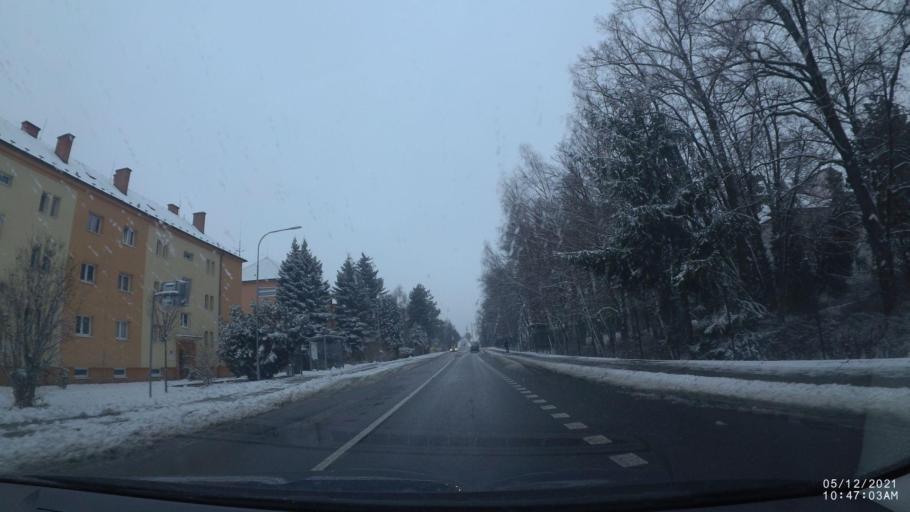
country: CZ
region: Kralovehradecky
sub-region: Okres Rychnov nad Kneznou
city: Rychnov nad Kneznou
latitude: 50.1687
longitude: 16.2696
